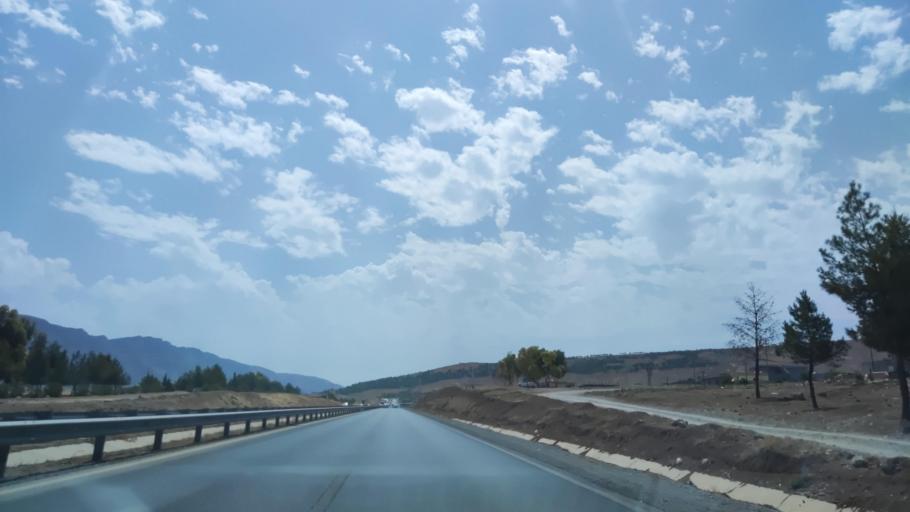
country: IQ
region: Arbil
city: Shaqlawah
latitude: 36.5021
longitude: 44.3562
